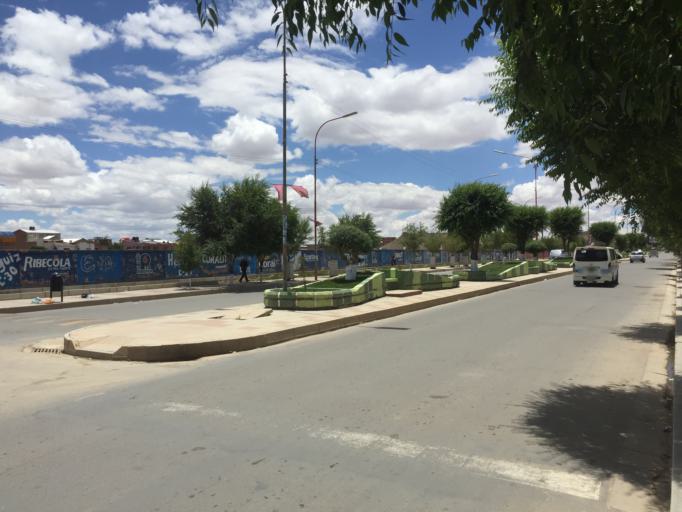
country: BO
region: Oruro
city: Oruro
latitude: -17.9819
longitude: -67.1326
